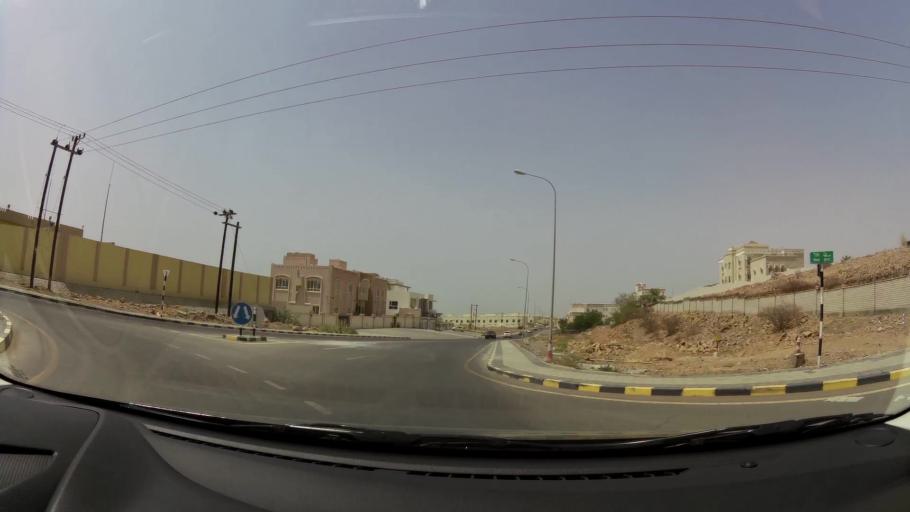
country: OM
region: Muhafazat Masqat
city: Bawshar
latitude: 23.5523
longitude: 58.3947
